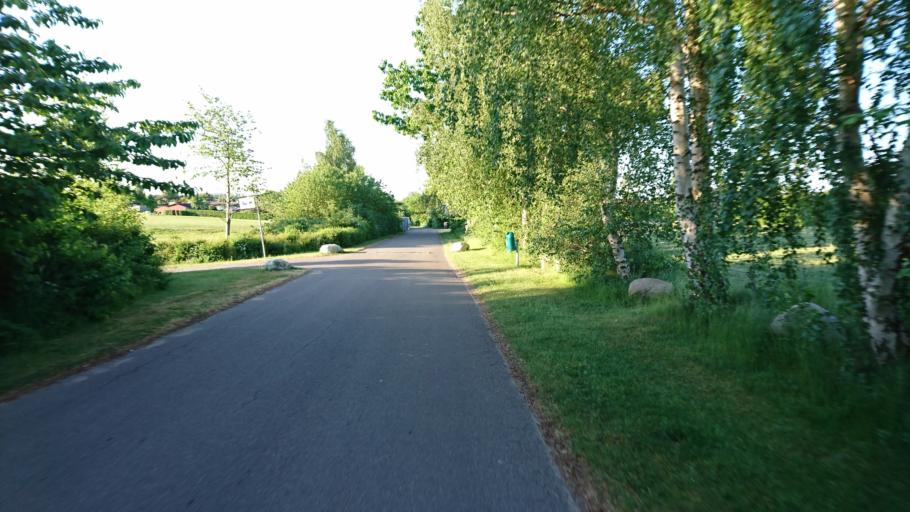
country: DK
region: Capital Region
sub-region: Ballerup Kommune
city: Ballerup
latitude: 55.7174
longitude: 12.3327
